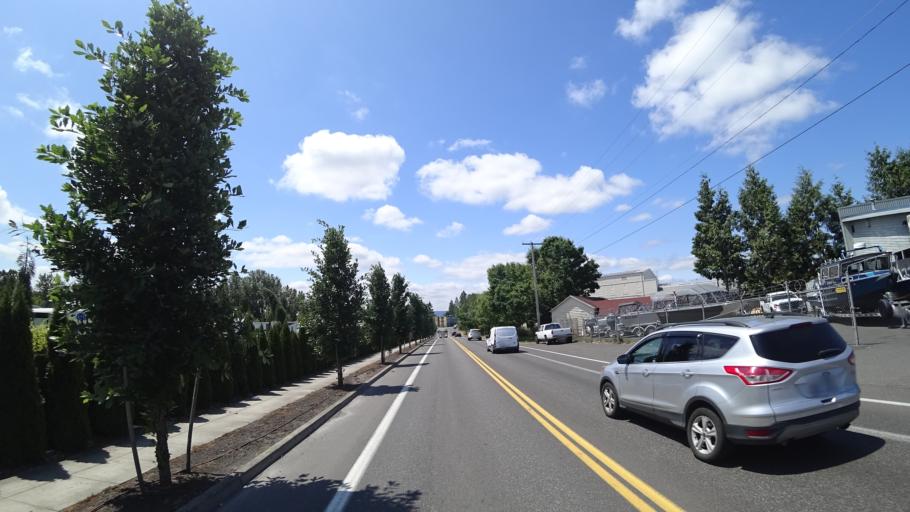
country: US
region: Washington
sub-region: Clark County
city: Vancouver
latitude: 45.6005
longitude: -122.6561
